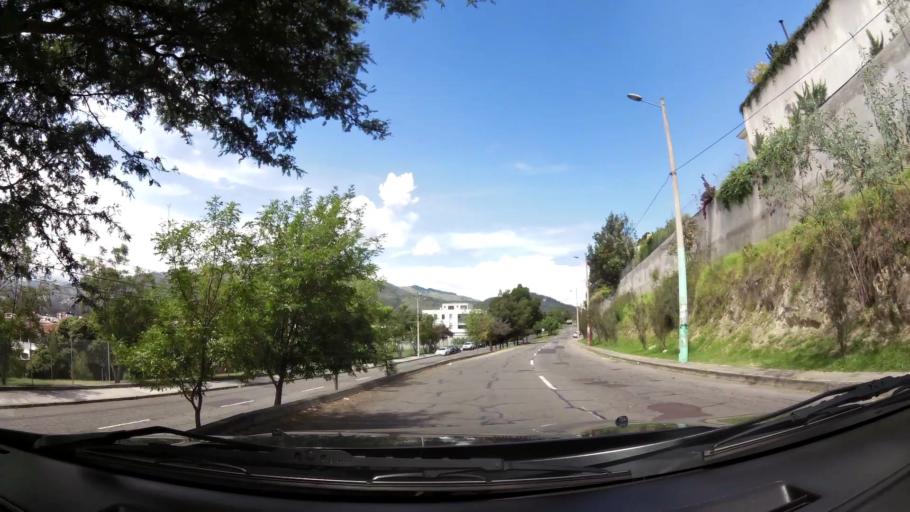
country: EC
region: Pichincha
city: Quito
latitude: -0.2094
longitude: -78.4282
